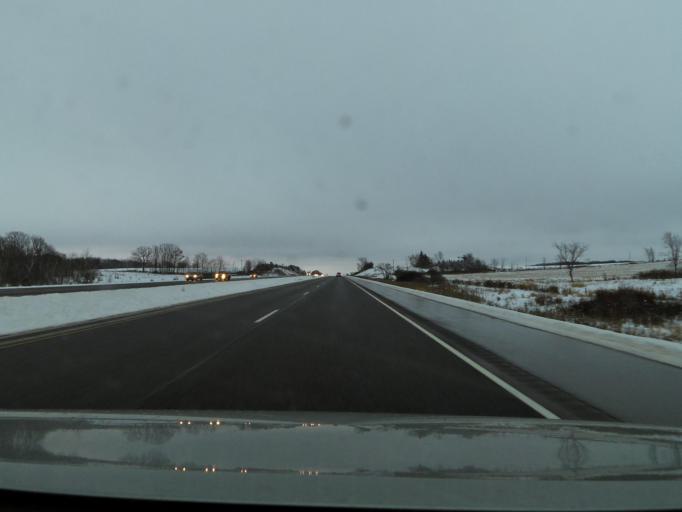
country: US
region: Wisconsin
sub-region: Saint Croix County
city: Woodville
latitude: 44.9336
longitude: -92.2212
